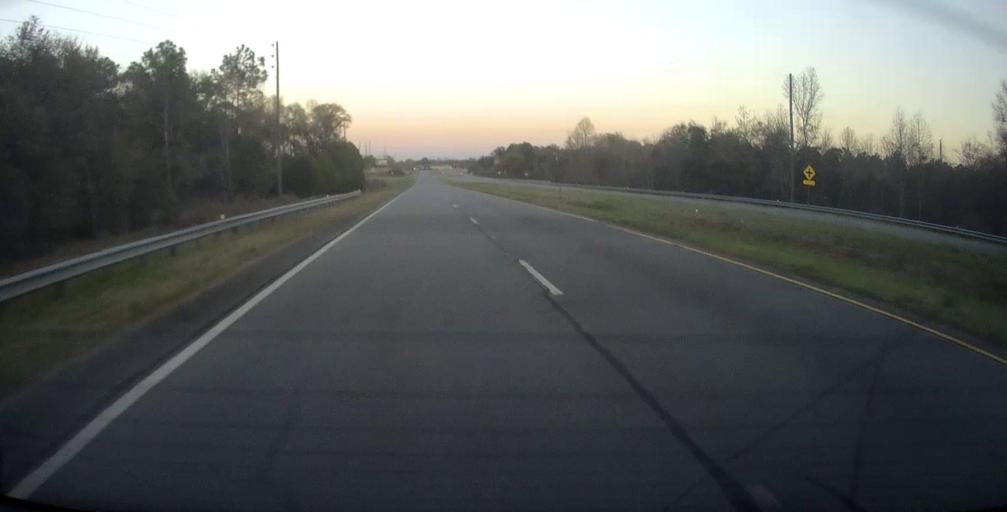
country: US
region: Georgia
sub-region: Dodge County
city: Eastman
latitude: 32.1763
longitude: -83.1709
